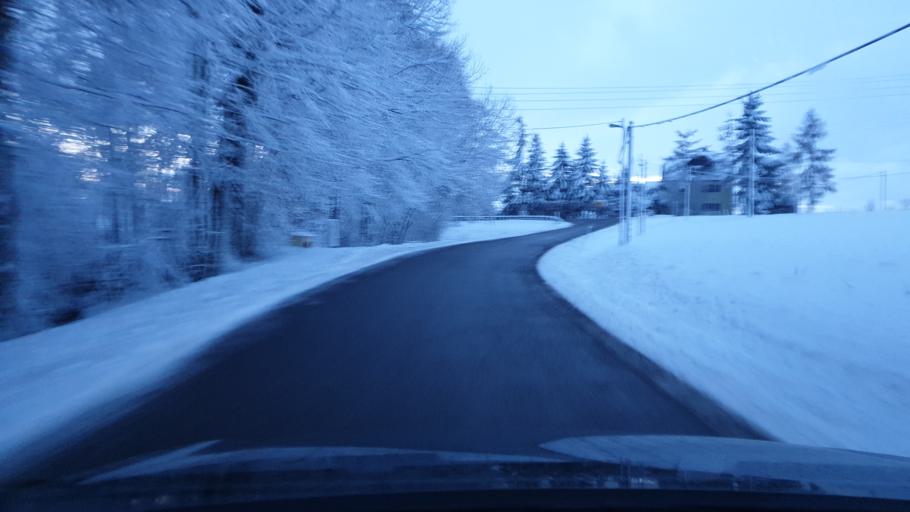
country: DE
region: Saxony
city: Altmittweida
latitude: 50.9826
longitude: 12.9331
